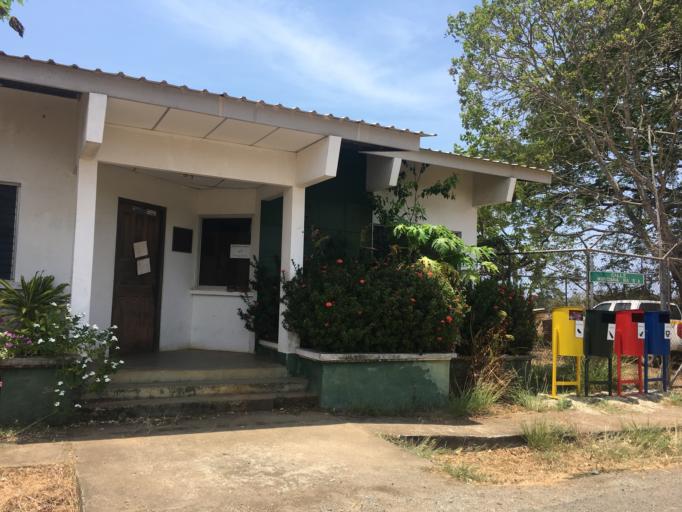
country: PA
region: Los Santos
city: Pedasi
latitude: 7.5271
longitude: -80.0264
